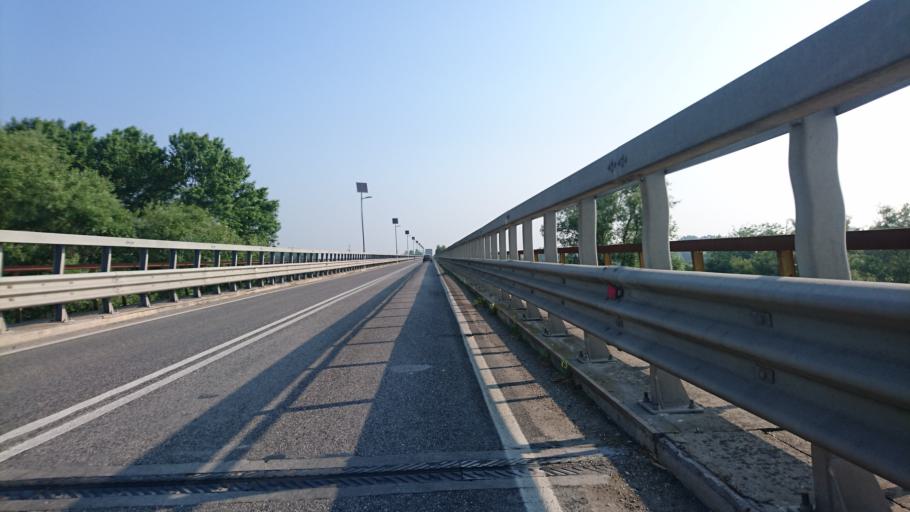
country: IT
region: Veneto
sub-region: Provincia di Rovigo
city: Castelnovo Bariano
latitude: 45.0174
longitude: 11.2909
